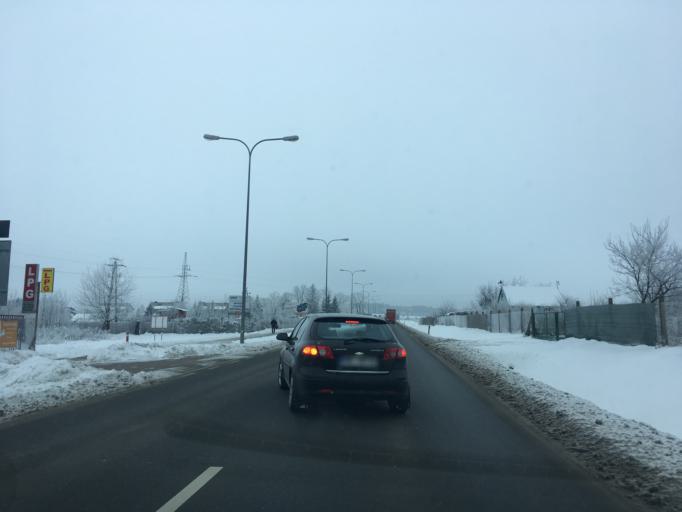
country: PL
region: Warmian-Masurian Voivodeship
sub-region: Powiat dzialdowski
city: Dzialdowo
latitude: 53.2489
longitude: 20.1906
